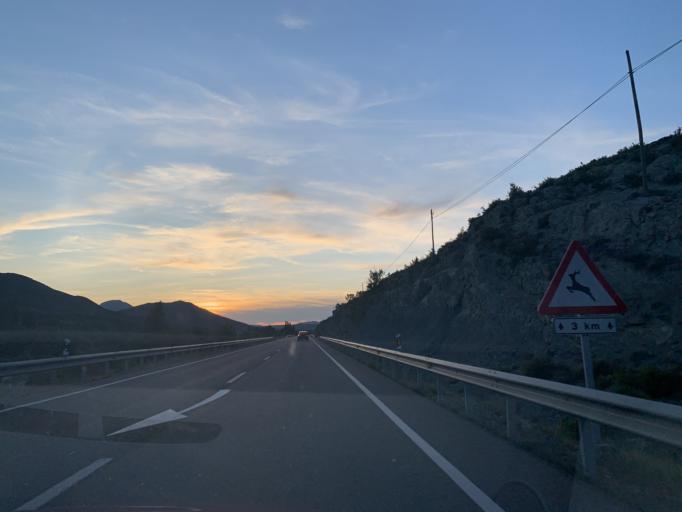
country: ES
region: Aragon
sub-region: Provincia de Huesca
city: Yebra de Basa
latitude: 42.4909
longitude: -0.3189
